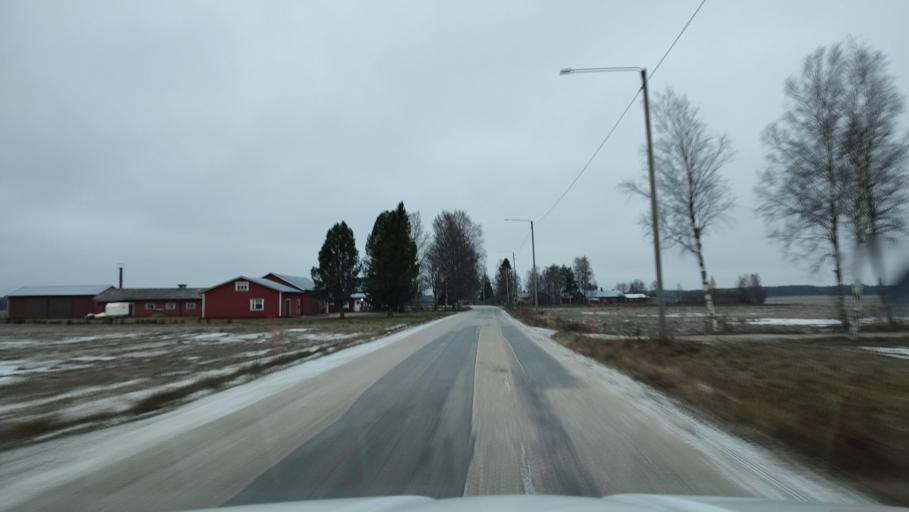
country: FI
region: Southern Ostrobothnia
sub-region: Suupohja
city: Karijoki
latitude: 62.2705
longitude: 21.6872
